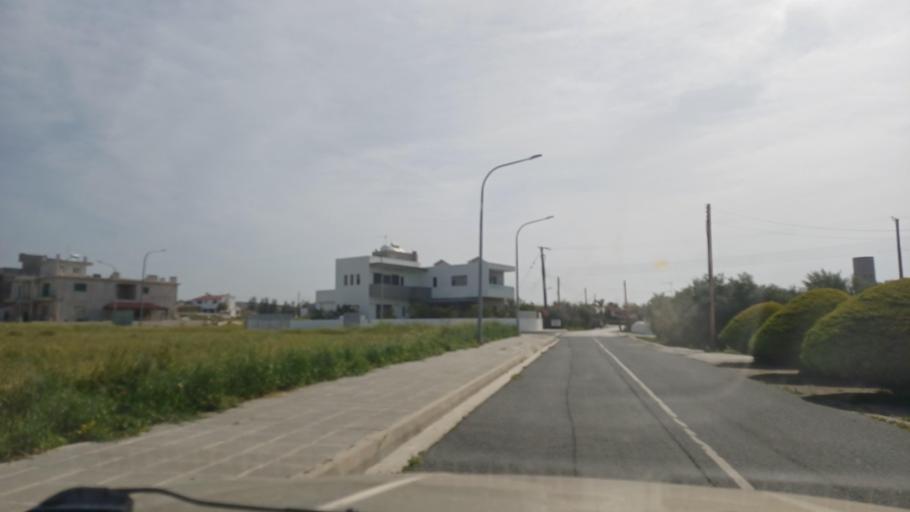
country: CY
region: Pafos
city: Paphos
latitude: 34.7540
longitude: 32.4666
